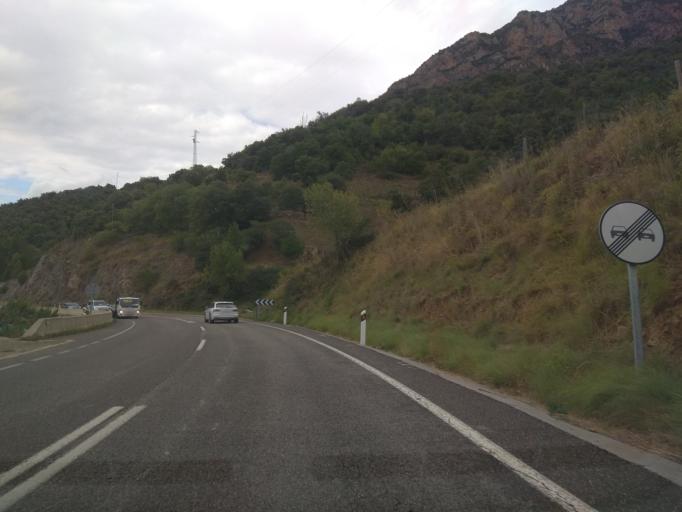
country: ES
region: Catalonia
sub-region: Provincia de Lleida
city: el Pont de Bar
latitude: 42.3622
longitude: 1.5740
